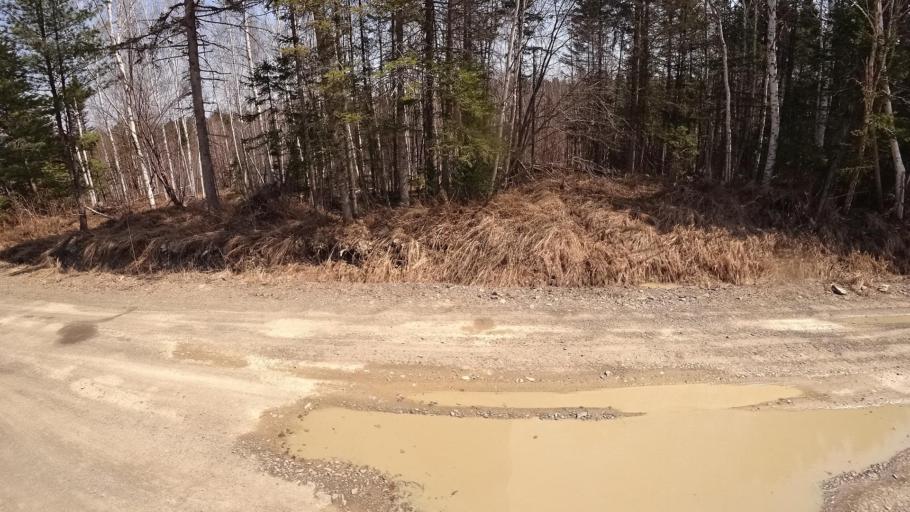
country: RU
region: Khabarovsk Krai
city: Selikhino
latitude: 50.6232
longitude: 137.4002
